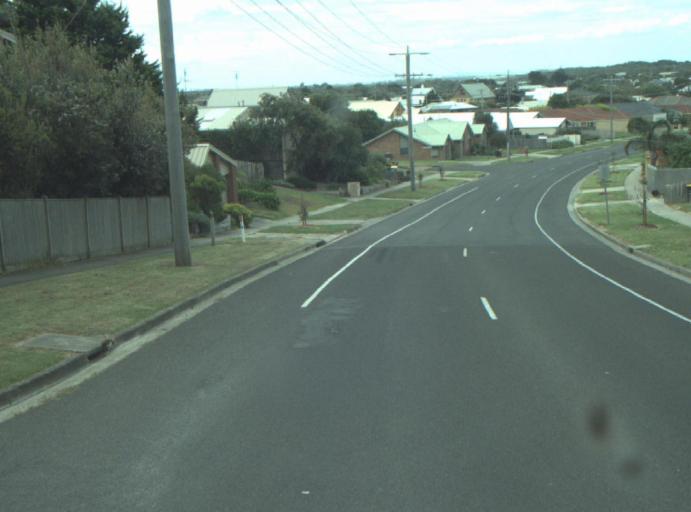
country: AU
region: Victoria
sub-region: Greater Geelong
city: Leopold
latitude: -38.2671
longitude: 144.5358
